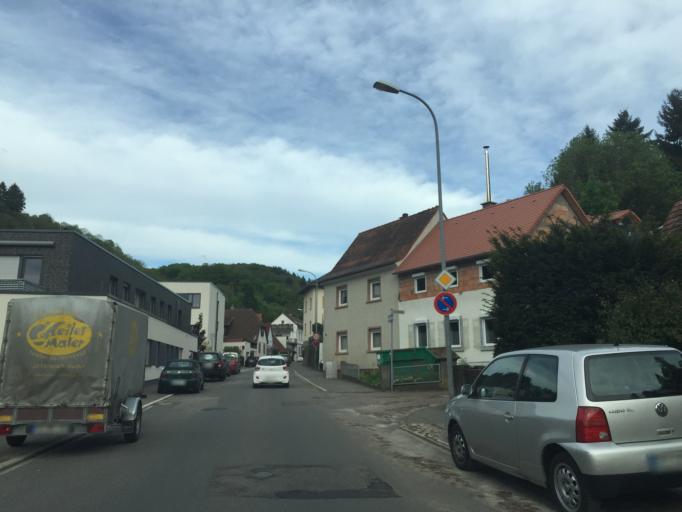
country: DE
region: Baden-Wuerttemberg
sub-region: Karlsruhe Region
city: Weinheim
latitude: 49.5436
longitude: 8.6765
